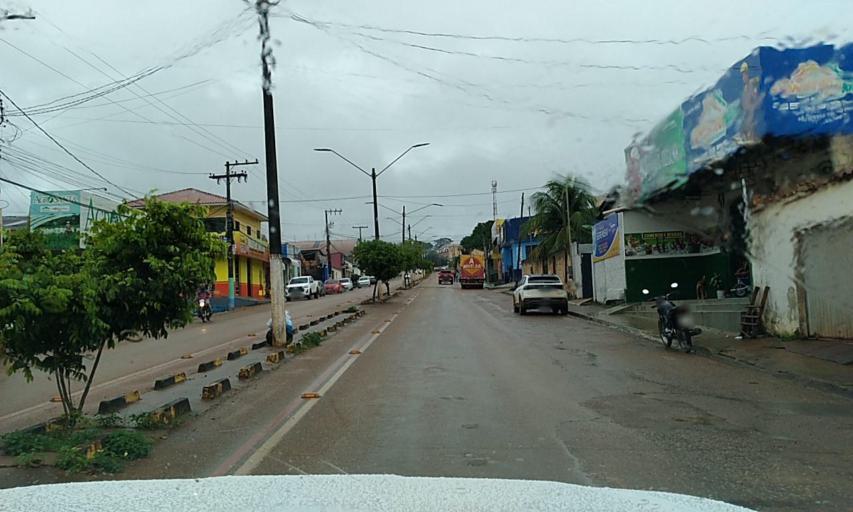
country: BR
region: Para
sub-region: Altamira
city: Altamira
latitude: -3.2124
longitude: -52.2295
